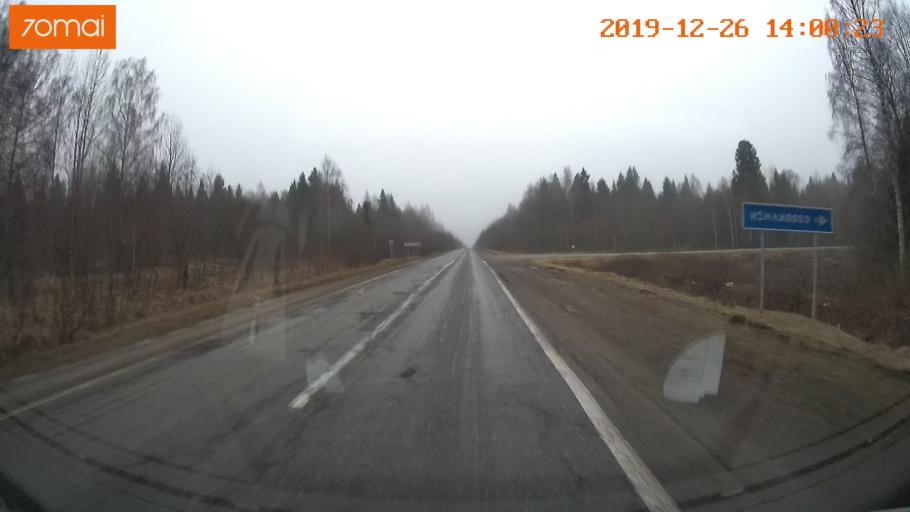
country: RU
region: Jaroslavl
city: Poshekhon'ye
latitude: 58.5586
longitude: 38.7423
